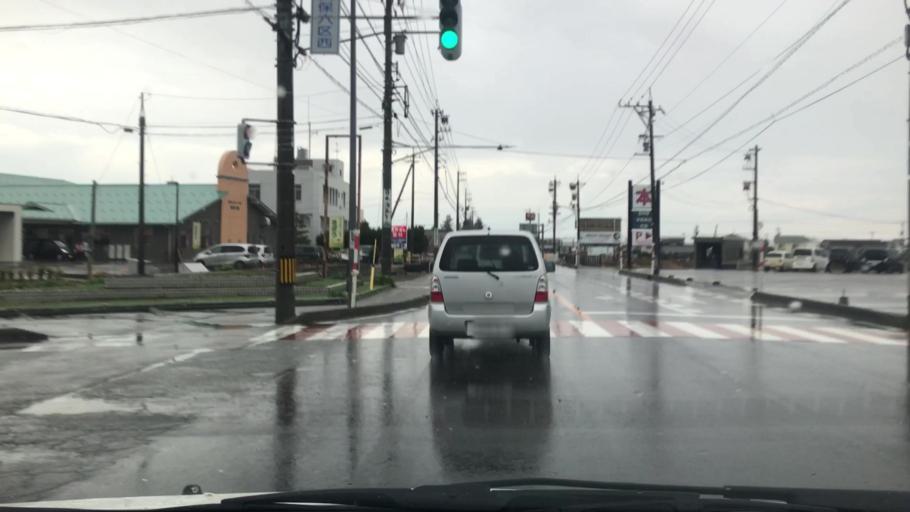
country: JP
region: Toyama
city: Yatsuomachi-higashikumisaka
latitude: 36.5988
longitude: 137.2035
